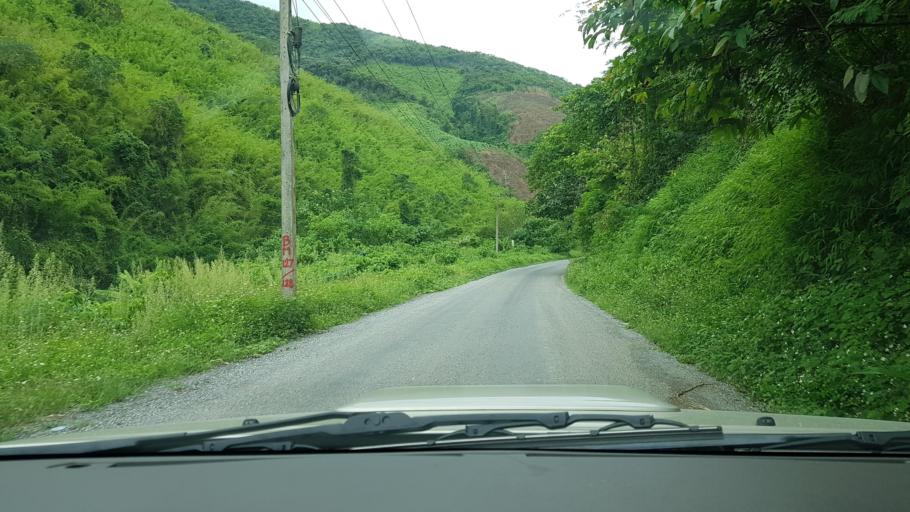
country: LA
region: Oudomxai
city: Muang La
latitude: 21.0435
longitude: 102.2413
